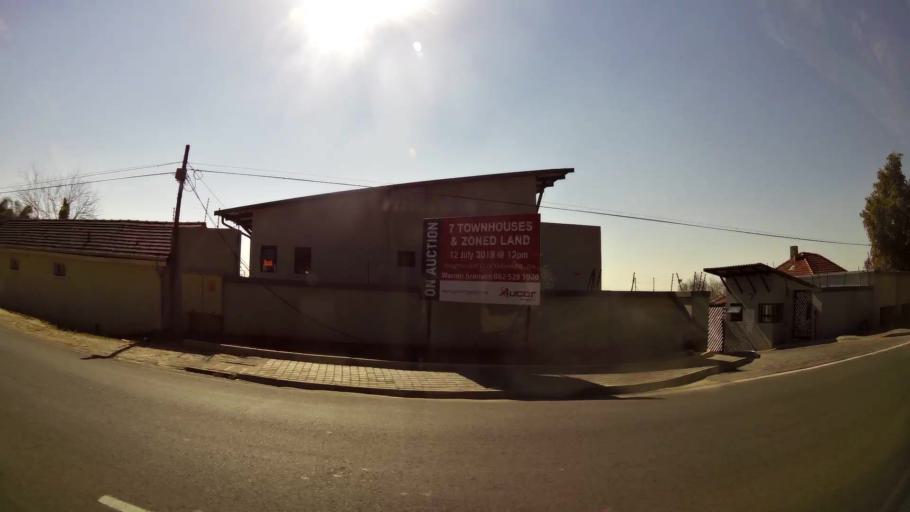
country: ZA
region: Gauteng
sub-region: City of Johannesburg Metropolitan Municipality
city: Johannesburg
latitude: -26.1646
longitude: 28.0925
